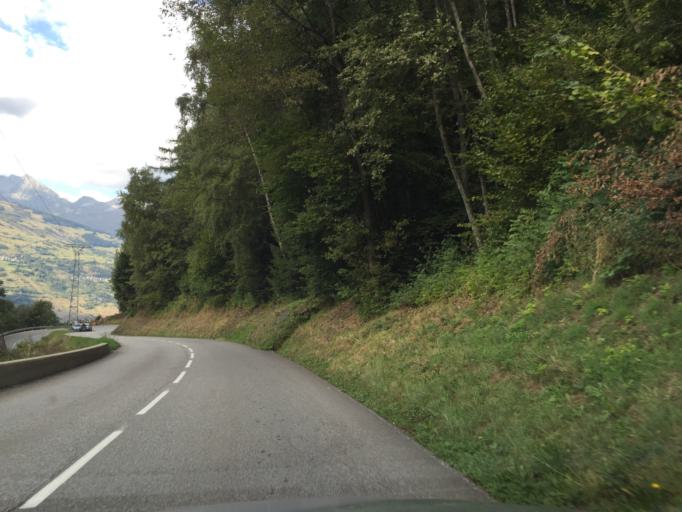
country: FR
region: Rhone-Alpes
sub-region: Departement de la Savoie
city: Belle-Plagne
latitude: 45.5527
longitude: 6.7511
